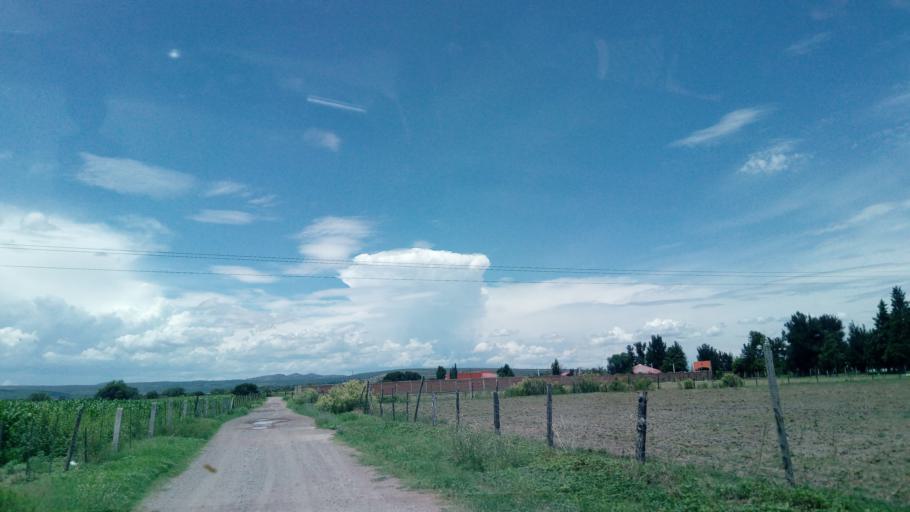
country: MX
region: Durango
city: Victoria de Durango
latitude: 24.0855
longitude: -104.5541
